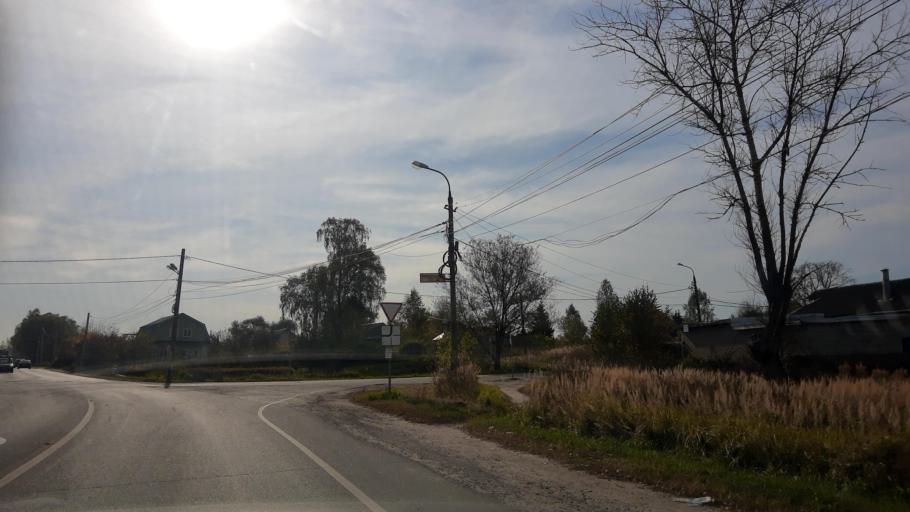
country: RU
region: Moskovskaya
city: Fryazevo
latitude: 55.7241
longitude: 38.4653
